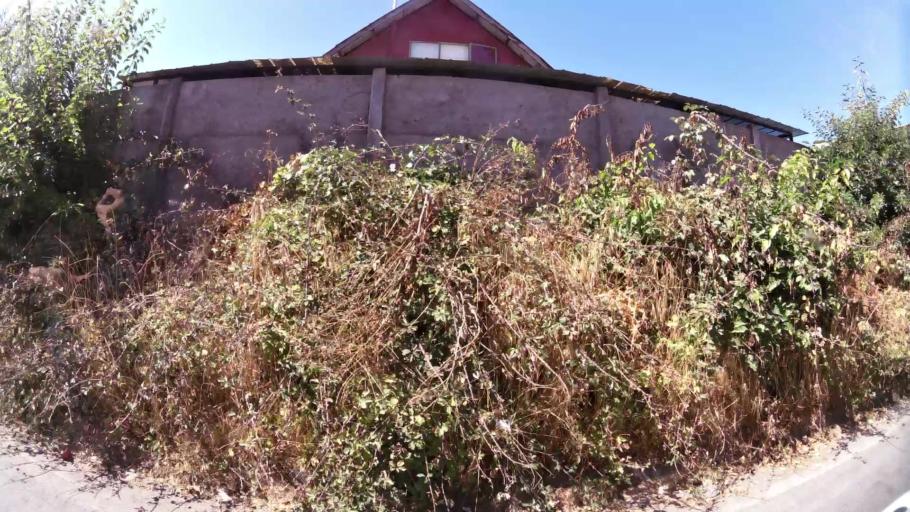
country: CL
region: O'Higgins
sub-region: Provincia de Colchagua
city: Chimbarongo
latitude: -34.5950
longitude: -70.9981
